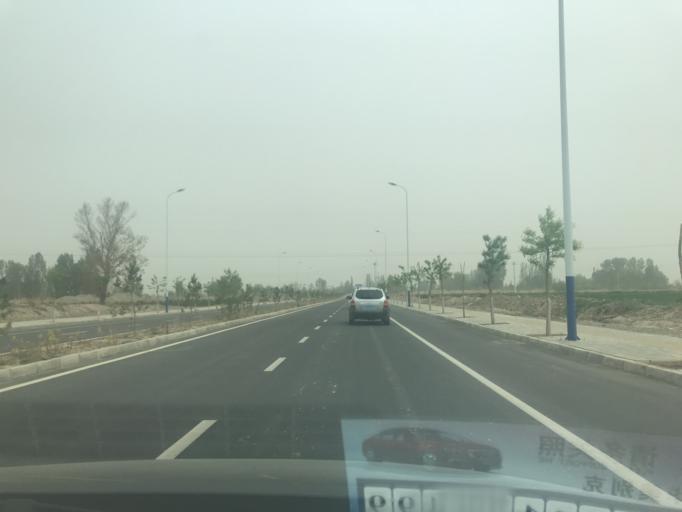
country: CN
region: Gansu Sheng
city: Gulang
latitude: 37.6939
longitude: 102.8592
